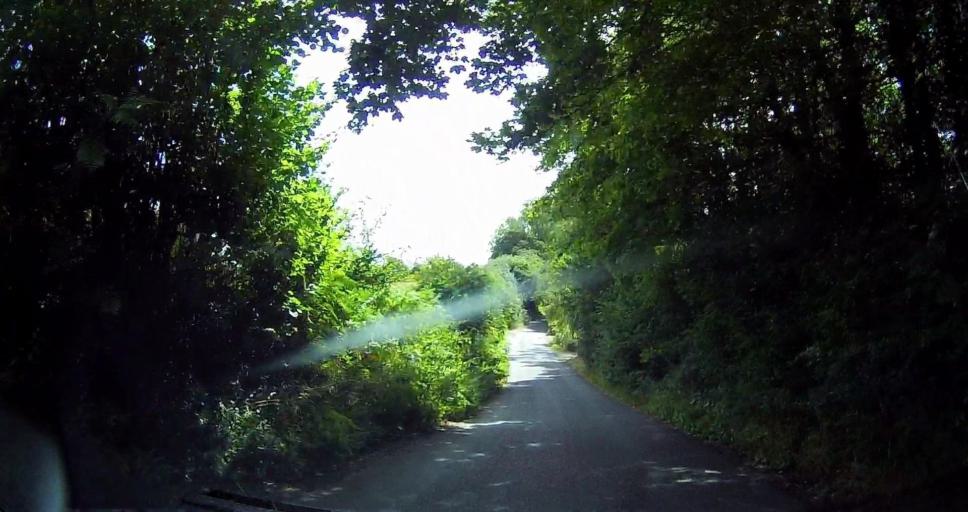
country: GB
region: England
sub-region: Kent
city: Borough Green
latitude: 51.2816
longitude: 0.3169
